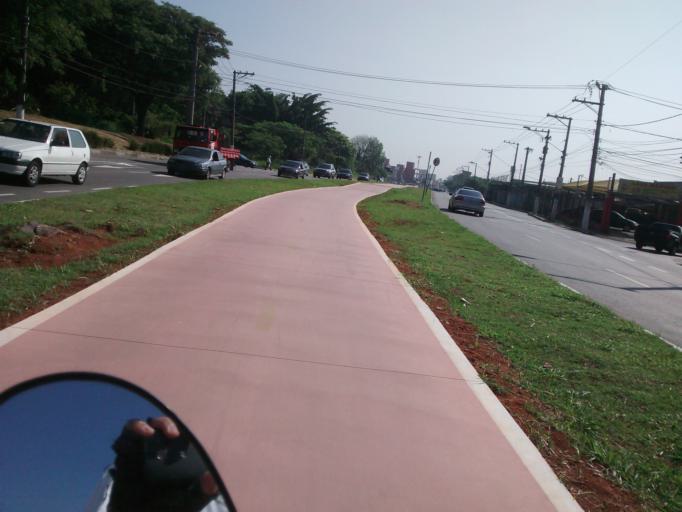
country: BR
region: Sao Paulo
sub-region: Taboao Da Serra
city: Taboao da Serra
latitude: -23.5926
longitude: -46.7407
